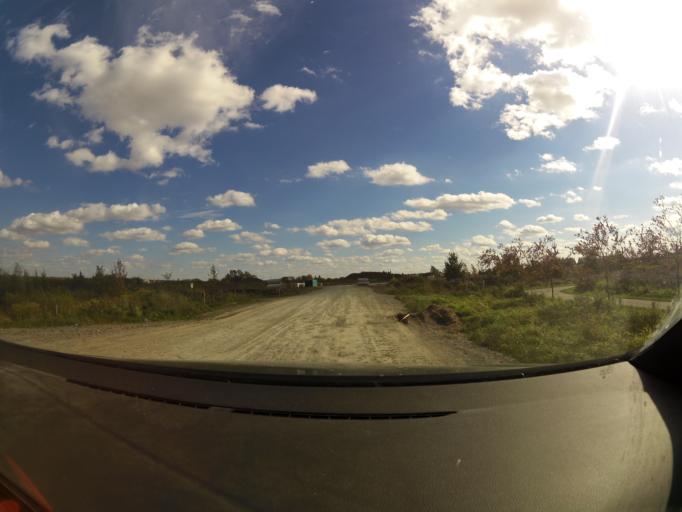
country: CA
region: Ontario
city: Bells Corners
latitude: 45.2736
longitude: -75.8836
